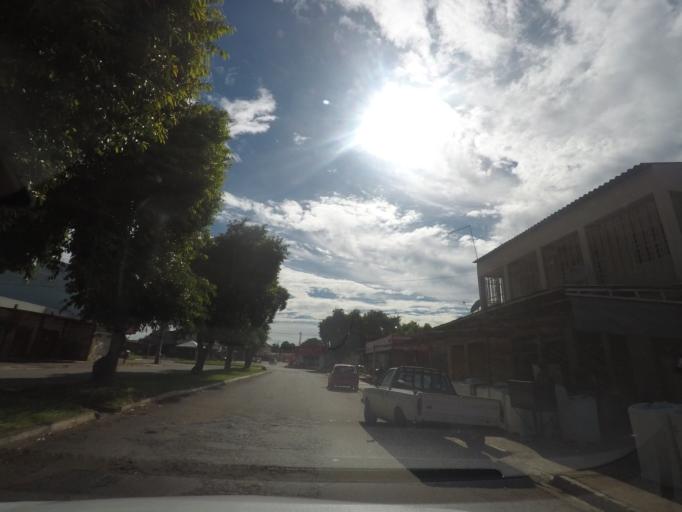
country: BR
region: Goias
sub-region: Aparecida De Goiania
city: Aparecida de Goiania
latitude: -16.8247
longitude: -49.2904
